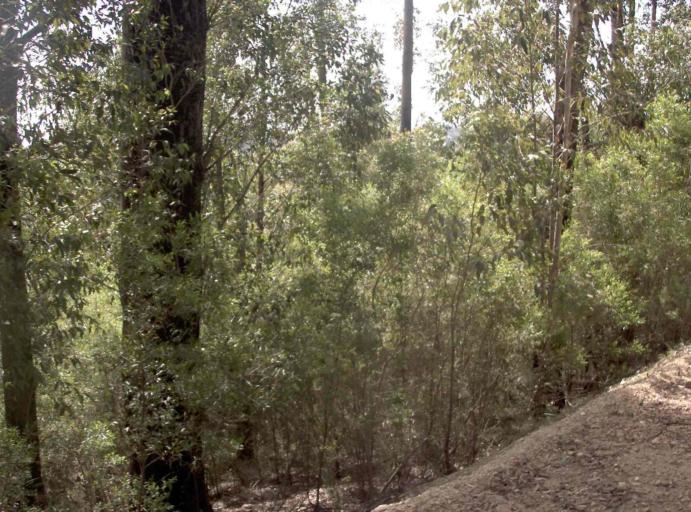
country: AU
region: Victoria
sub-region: East Gippsland
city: Lakes Entrance
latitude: -37.6155
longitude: 148.6987
